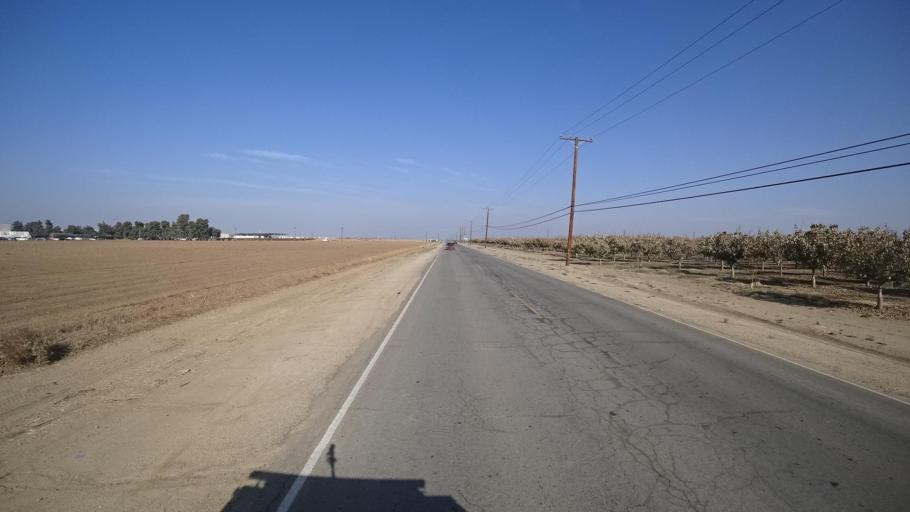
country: US
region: California
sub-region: Kern County
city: McFarland
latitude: 35.7012
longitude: -119.2230
